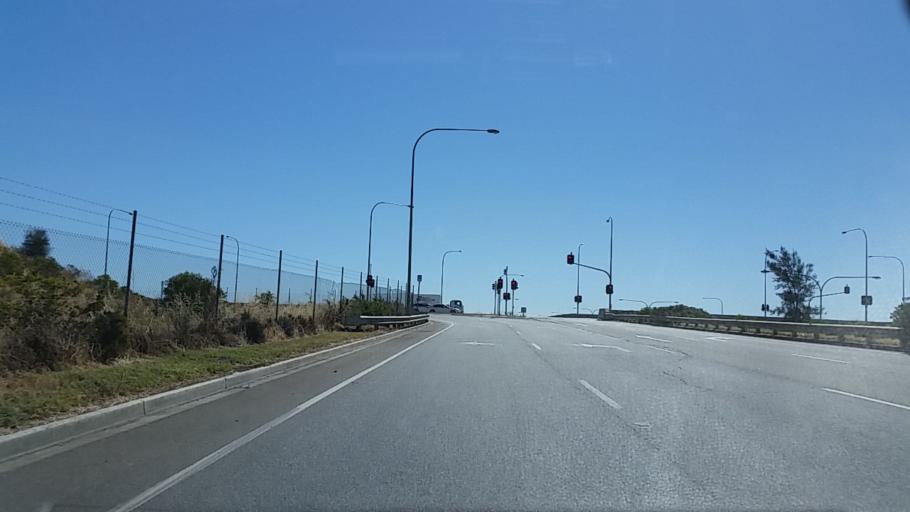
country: AU
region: South Australia
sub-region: Port Adelaide Enfield
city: Alberton
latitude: -34.8339
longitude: 138.5467
